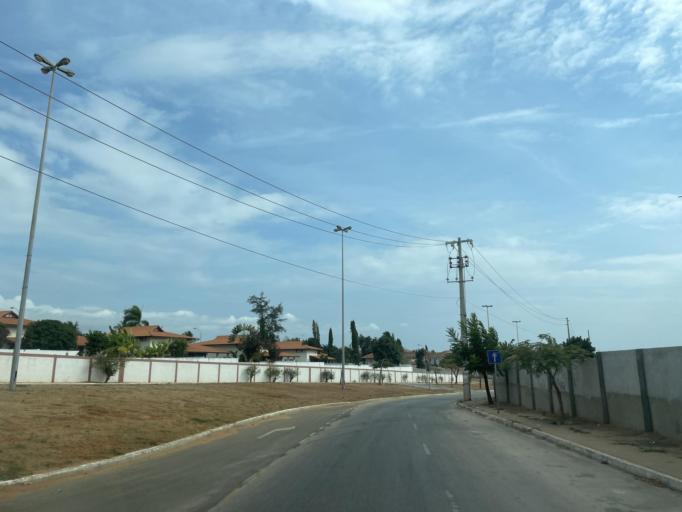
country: AO
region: Luanda
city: Luanda
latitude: -8.9243
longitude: 13.1792
